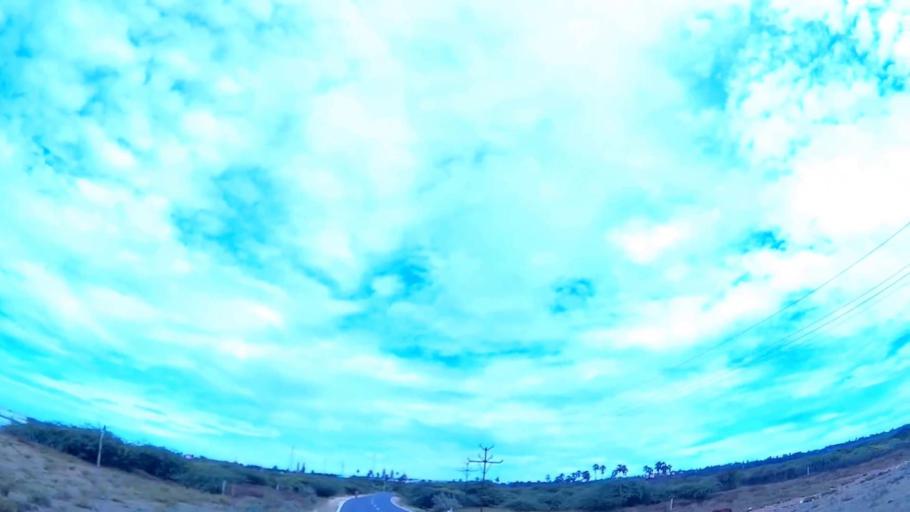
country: IN
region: Tamil Nadu
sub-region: Thoothukkudi
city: Udankudi
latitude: 8.3813
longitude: 78.0481
